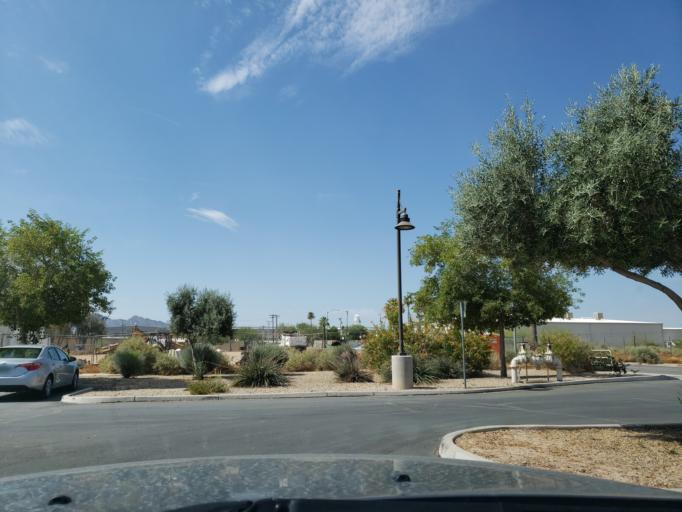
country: US
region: Arizona
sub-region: Maricopa County
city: Goodyear
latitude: 33.4385
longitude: -112.3600
